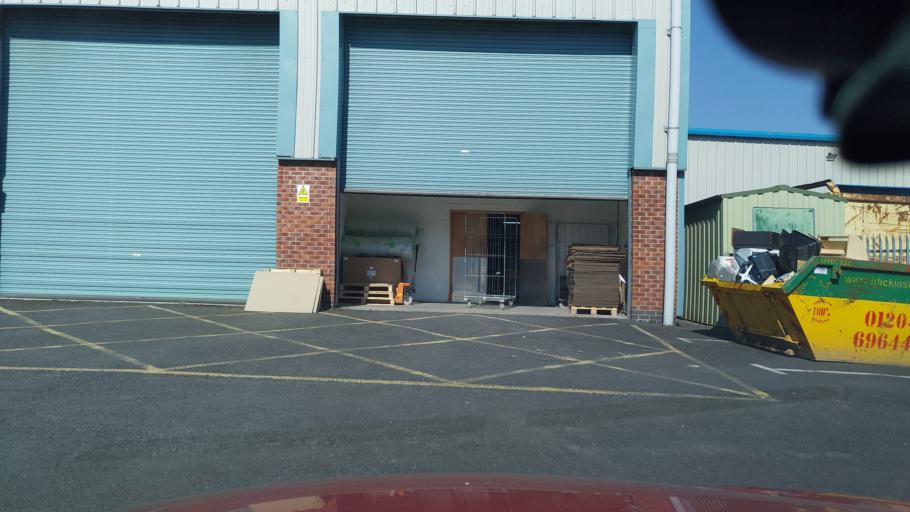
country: GB
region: England
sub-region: Borough of Bolton
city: Blackrod
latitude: 53.5944
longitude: -2.5661
